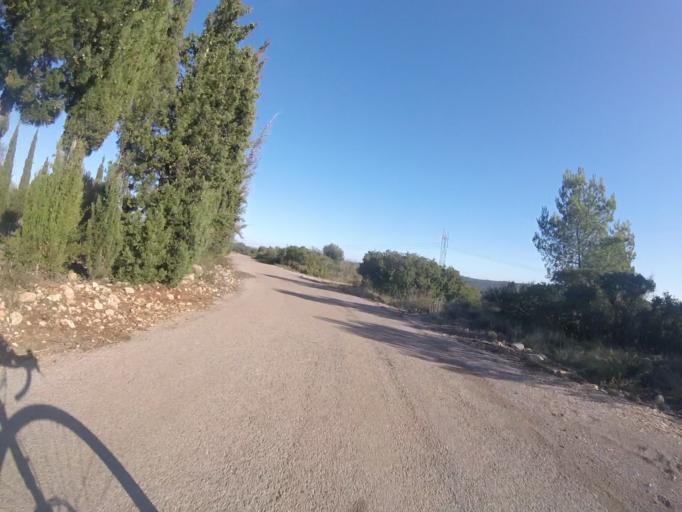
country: ES
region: Valencia
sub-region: Provincia de Castello
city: Cuevas de Vinroma
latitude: 40.2881
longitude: 0.0769
